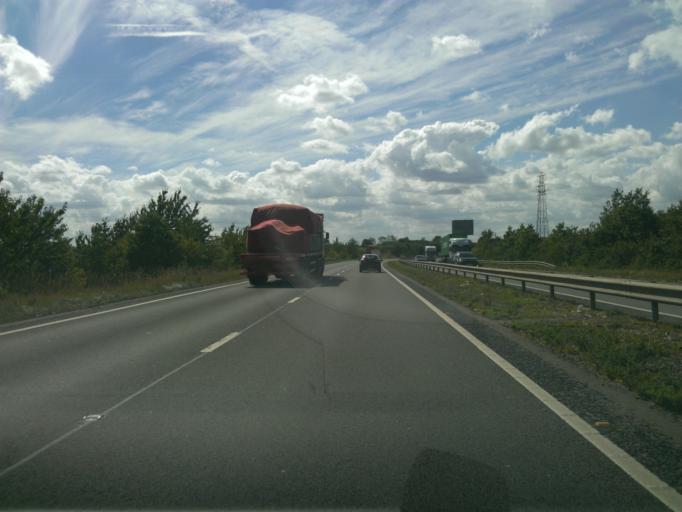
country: GB
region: England
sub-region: Northamptonshire
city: Burton Latimer
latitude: 52.3793
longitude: -0.6533
